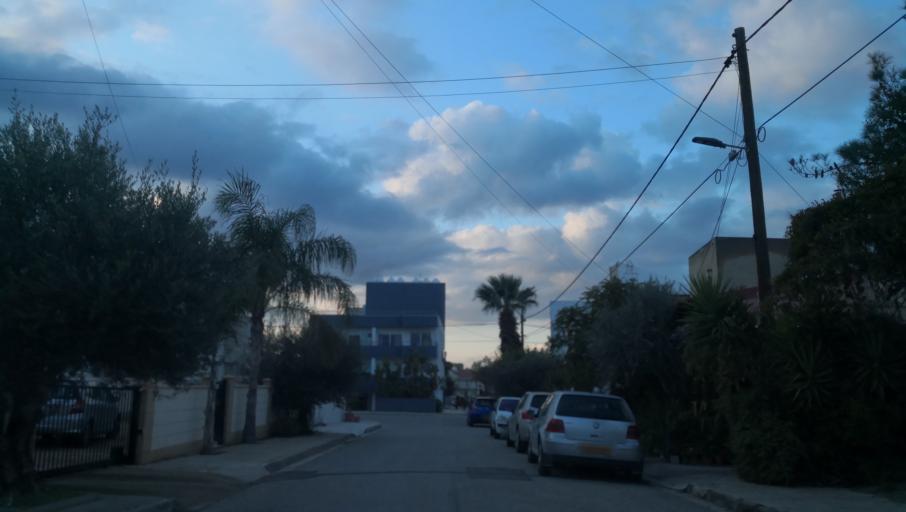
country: CY
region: Lefkosia
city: Kato Deftera
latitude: 35.0991
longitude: 33.2996
